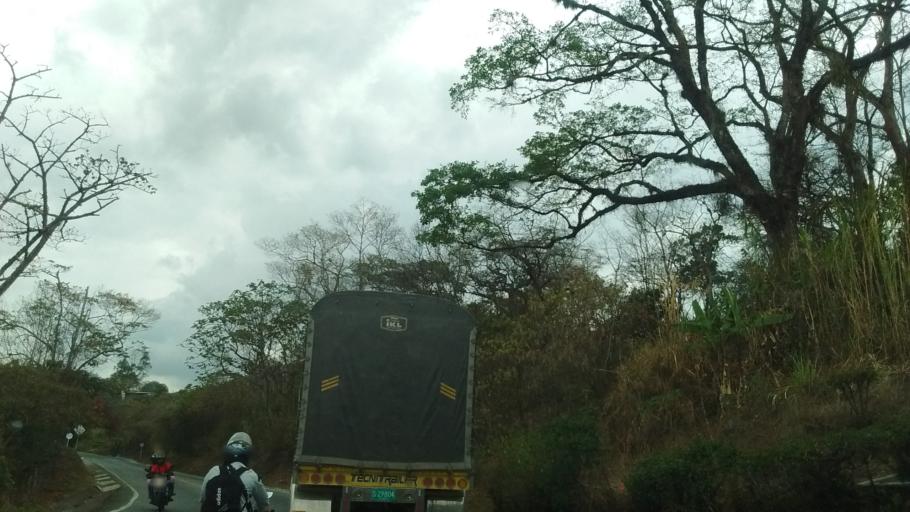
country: CO
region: Cauca
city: Rosas
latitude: 2.2761
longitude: -76.7201
